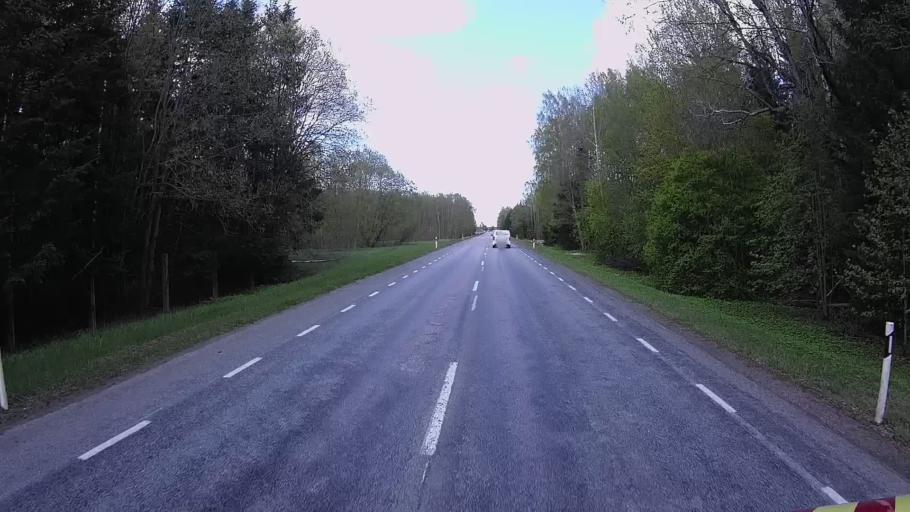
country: EE
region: Tartu
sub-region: Alatskivi vald
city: Kallaste
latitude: 58.5127
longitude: 26.9562
